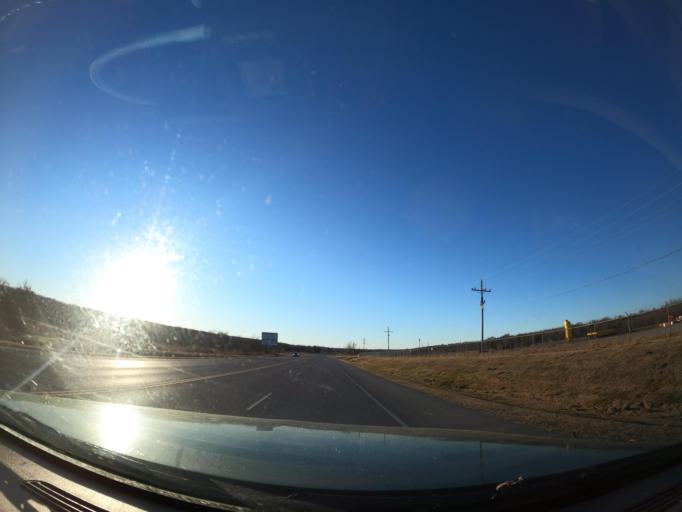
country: US
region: Oklahoma
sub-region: Pittsburg County
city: Krebs
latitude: 34.8947
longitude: -95.6619
